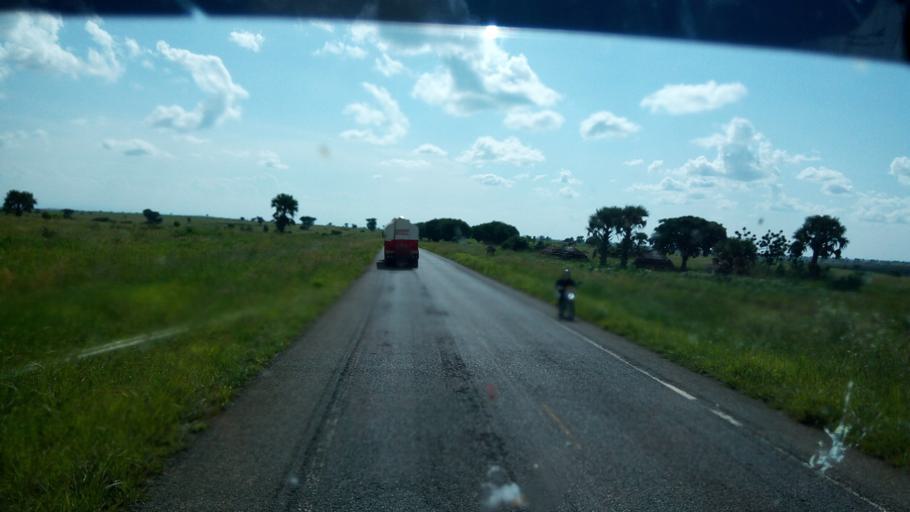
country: UG
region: Northern Region
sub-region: Nwoya District
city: Nwoya
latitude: 2.5604
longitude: 31.6904
